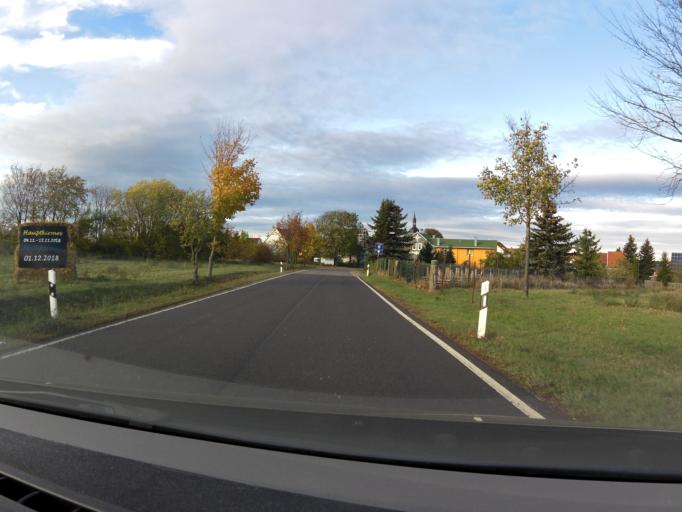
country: DE
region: Thuringia
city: Crawinkel
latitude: 50.7786
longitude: 10.7894
